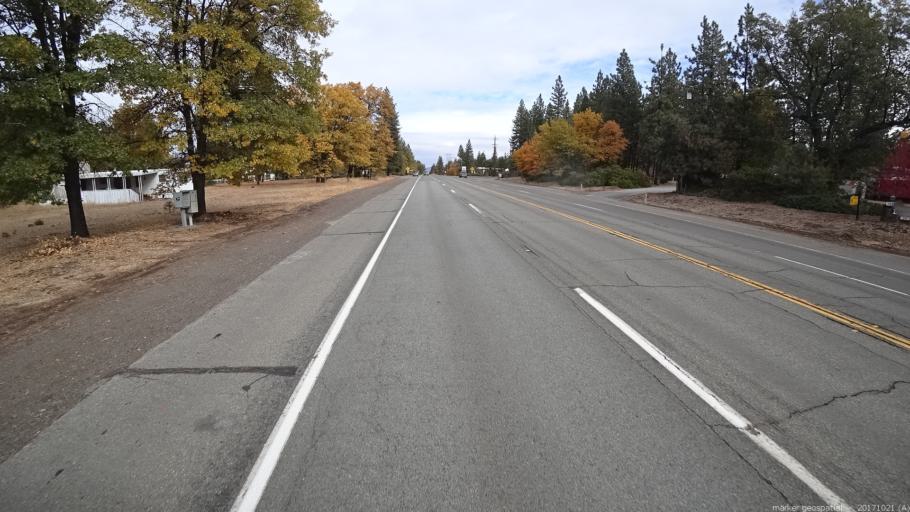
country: US
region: California
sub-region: Shasta County
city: Burney
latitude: 40.9224
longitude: -121.6228
